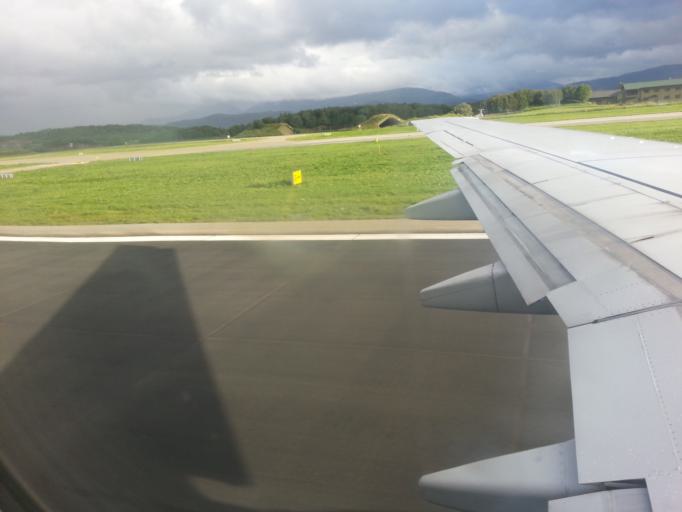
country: NO
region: Nordland
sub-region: Bodo
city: Bodo
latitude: 67.2704
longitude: 14.3796
